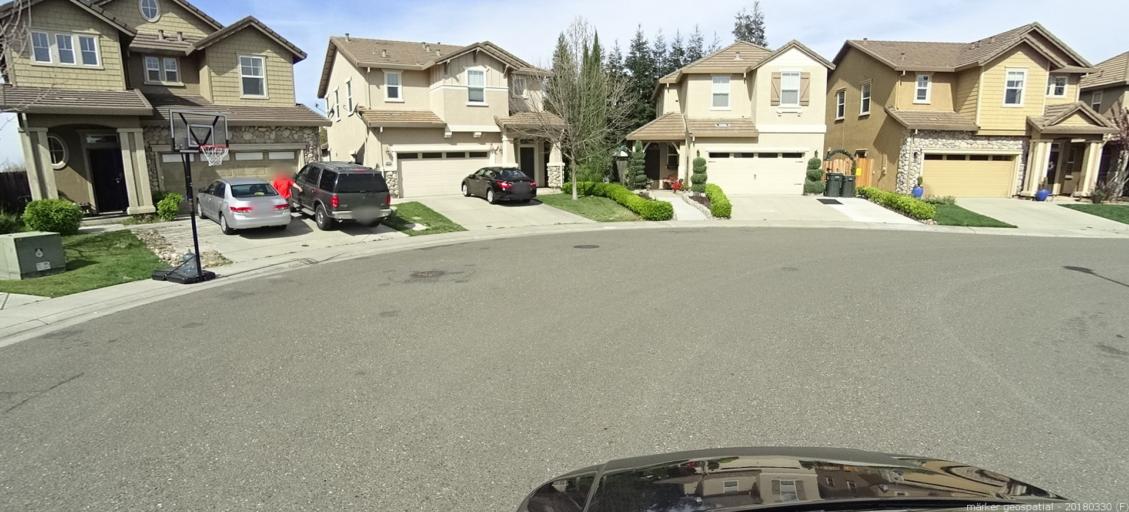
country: US
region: California
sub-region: Sacramento County
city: Rosemont
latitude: 38.5463
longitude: -121.3458
